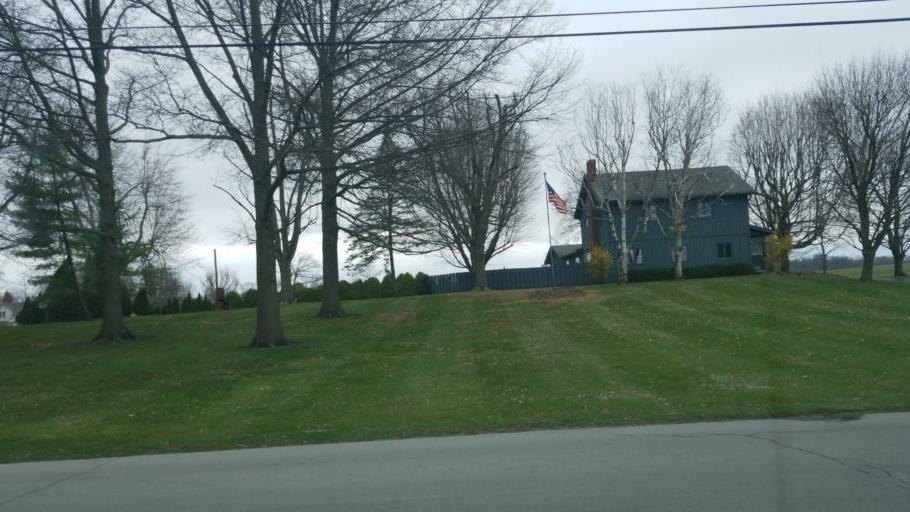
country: US
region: Ohio
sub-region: Wyandot County
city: Upper Sandusky
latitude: 40.8190
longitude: -83.1290
